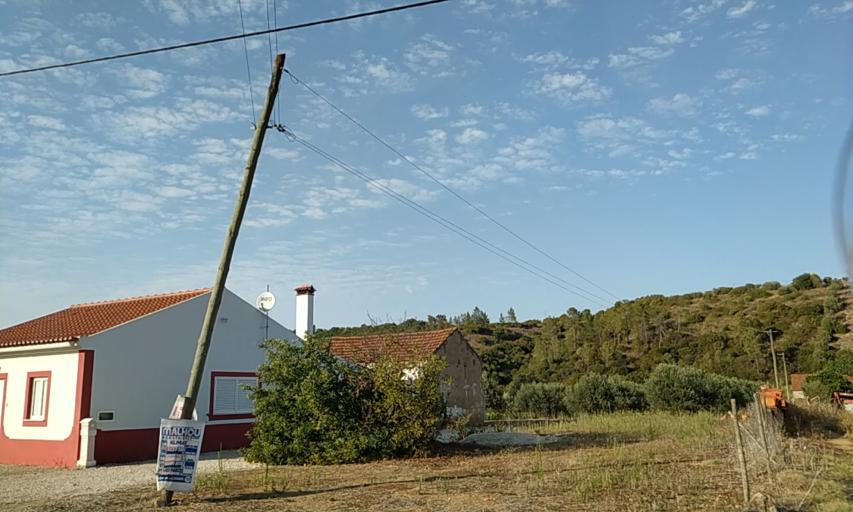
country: PT
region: Santarem
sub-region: Alcanena
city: Alcanena
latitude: 39.3614
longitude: -8.6526
